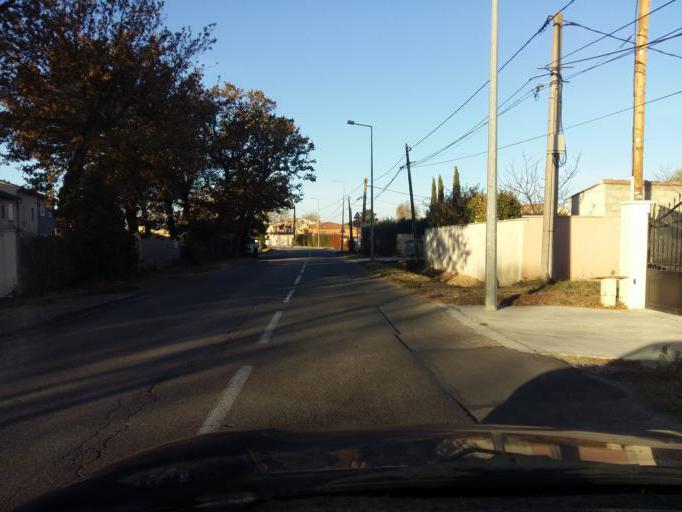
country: FR
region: Provence-Alpes-Cote d'Azur
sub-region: Departement du Vaucluse
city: Monteux
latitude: 44.0347
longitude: 4.9830
